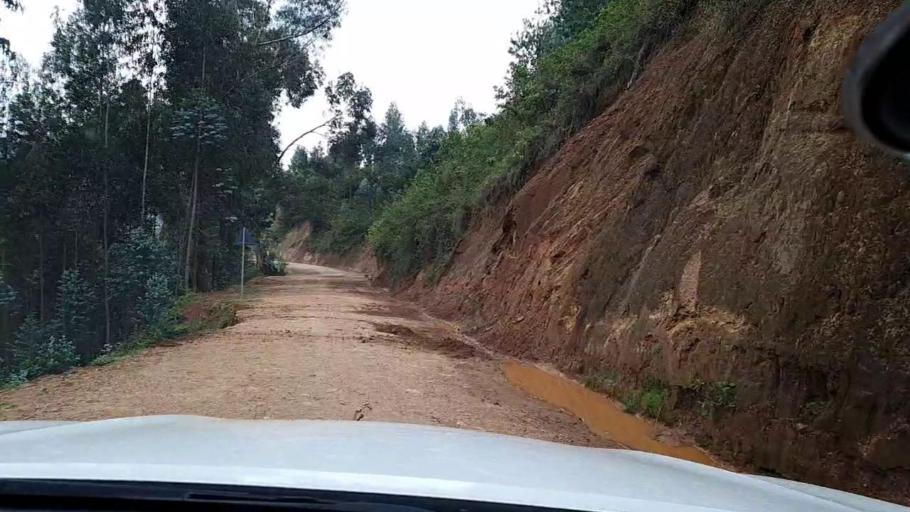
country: RW
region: Western Province
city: Kibuye
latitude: -2.2795
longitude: 29.3015
